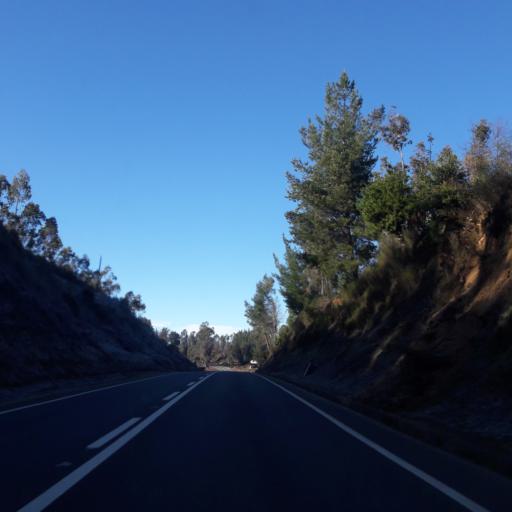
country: CL
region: Biobio
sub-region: Provincia de Biobio
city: La Laja
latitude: -37.3272
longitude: -72.9135
